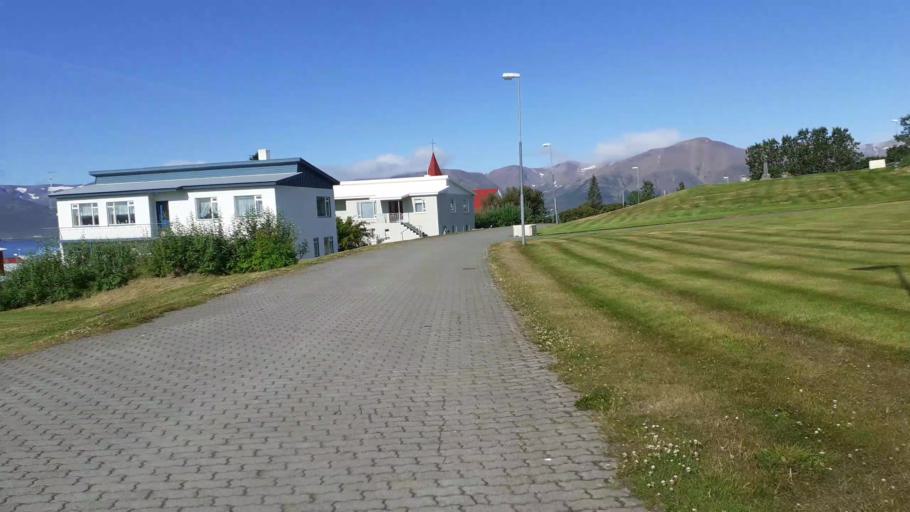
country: IS
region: Northeast
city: Dalvik
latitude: 65.9790
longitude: -18.3728
